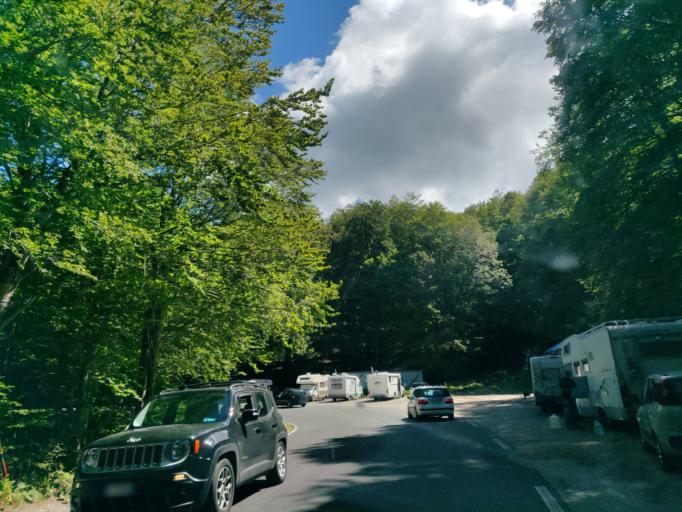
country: IT
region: Tuscany
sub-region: Provincia di Siena
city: Abbadia San Salvatore
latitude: 42.8903
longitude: 11.6094
